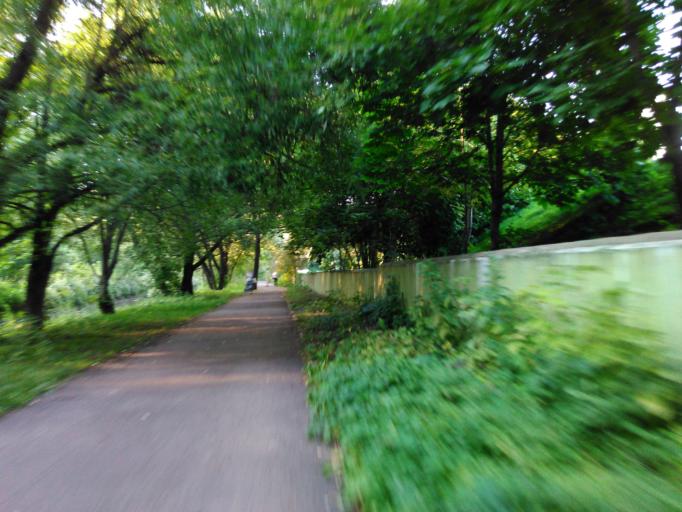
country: RU
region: Moscow
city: Vorob'yovo
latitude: 55.7265
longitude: 37.5191
